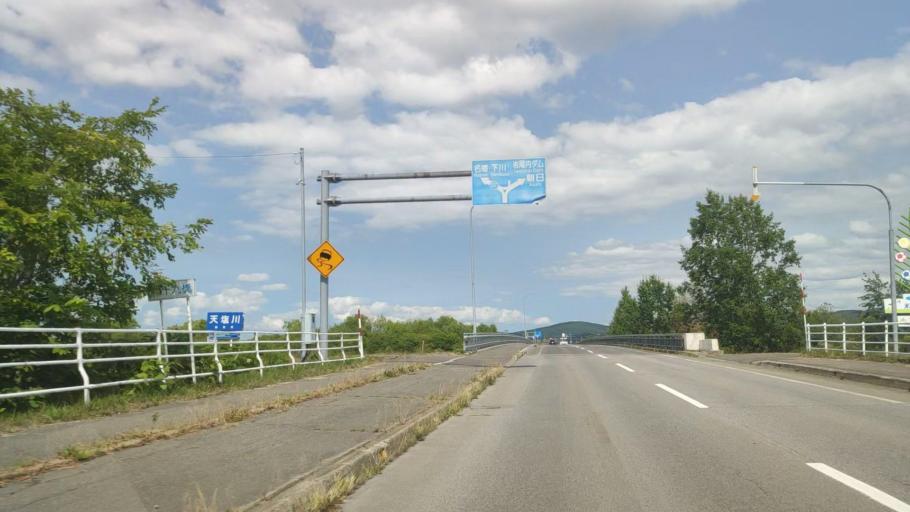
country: JP
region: Hokkaido
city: Nayoro
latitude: 44.1896
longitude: 142.4128
